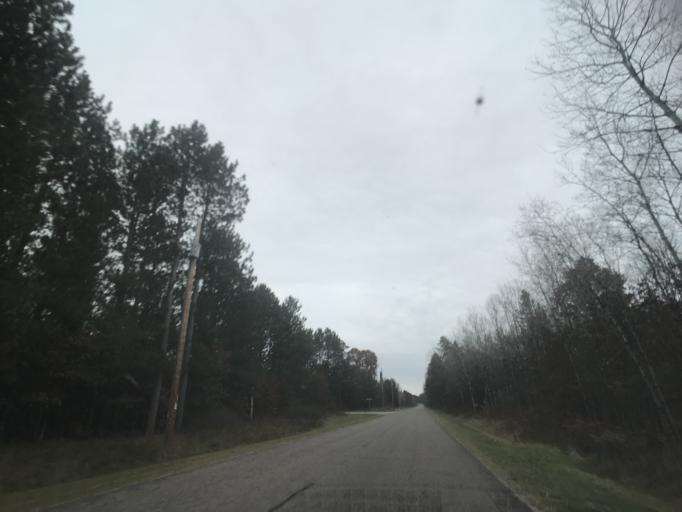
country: US
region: Wisconsin
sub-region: Oconto County
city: Gillett
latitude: 45.2793
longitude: -88.2570
